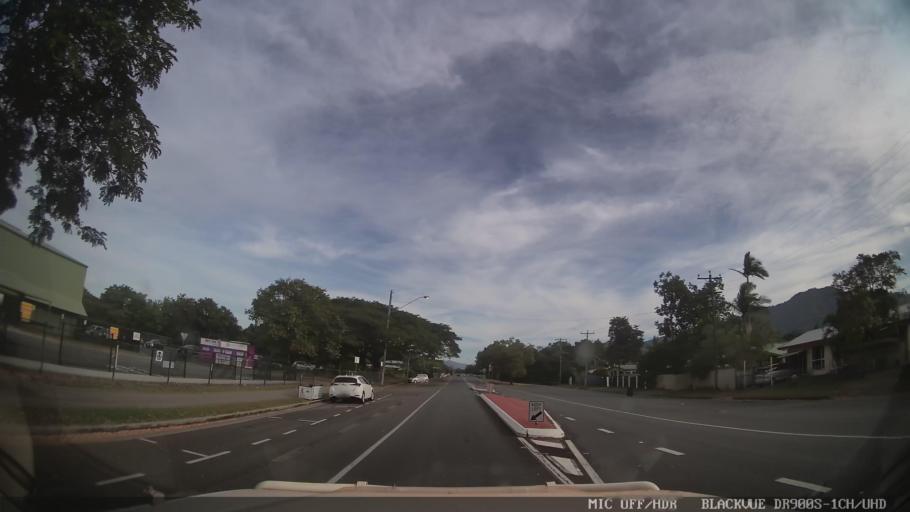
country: AU
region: Queensland
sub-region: Cairns
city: Cairns
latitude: -16.9066
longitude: 145.7428
